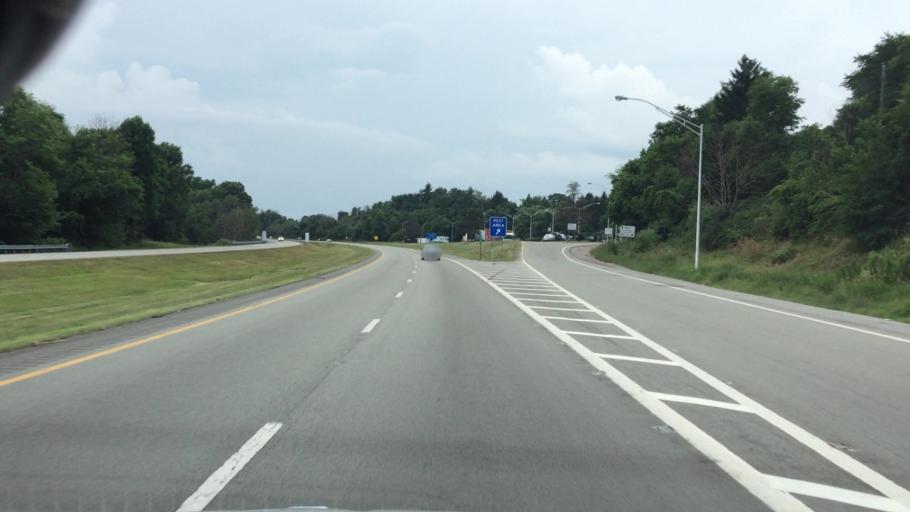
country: US
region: West Virginia
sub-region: Ohio County
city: West Liberty
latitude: 40.0924
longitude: -80.5327
